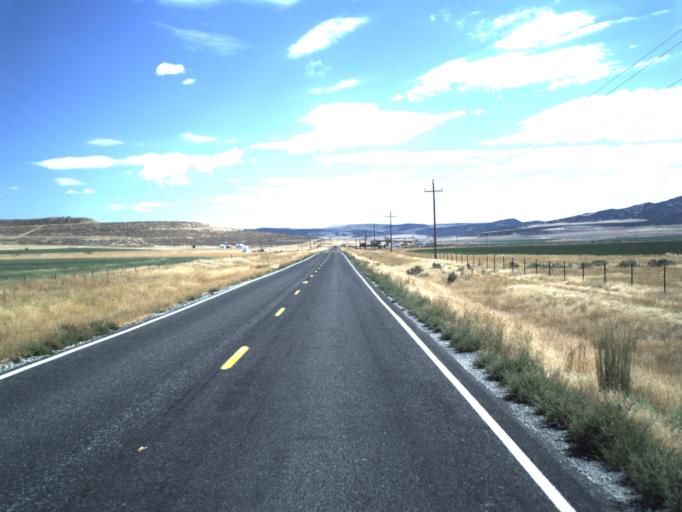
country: US
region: Idaho
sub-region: Oneida County
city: Malad City
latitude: 41.9666
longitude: -112.7819
